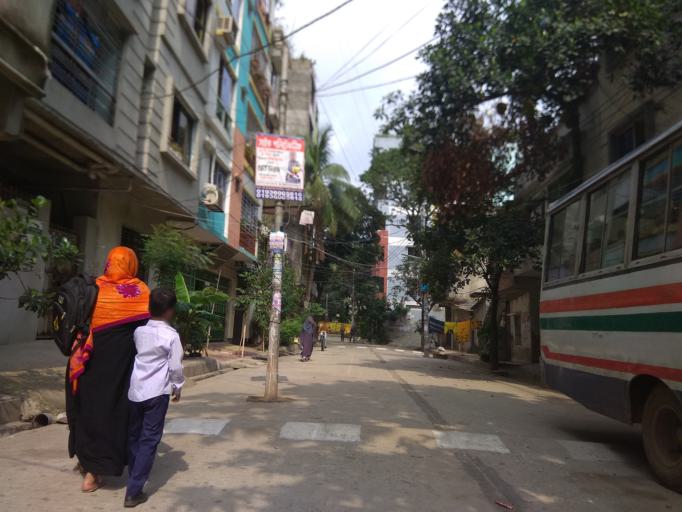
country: BD
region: Dhaka
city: Azimpur
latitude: 23.8083
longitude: 90.3651
